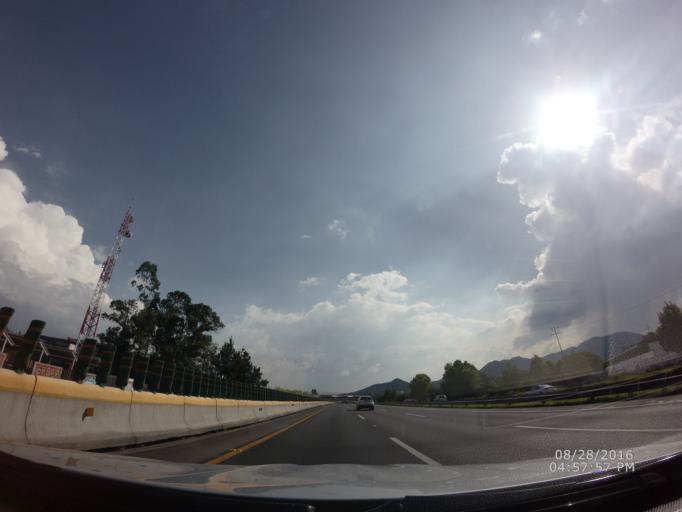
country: MX
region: Mexico
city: Ecatepec
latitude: 19.6123
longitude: -99.0332
